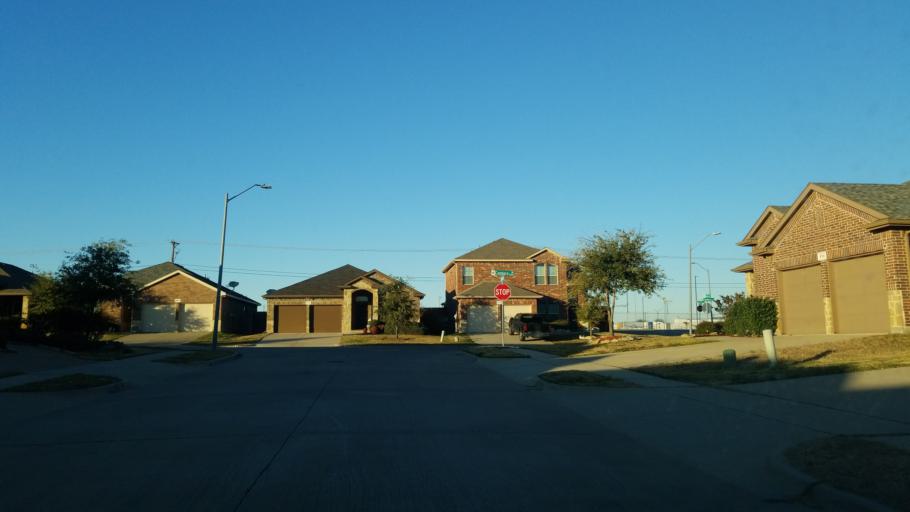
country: US
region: Texas
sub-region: Tarrant County
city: Arlington
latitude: 32.7344
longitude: -97.0530
